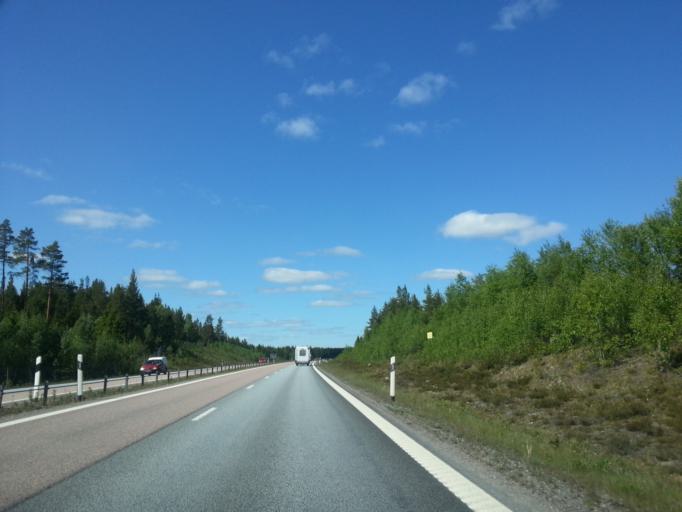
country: SE
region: Gaevleborg
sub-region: Soderhamns Kommun
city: Soderhamn
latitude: 61.4174
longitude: 16.9876
